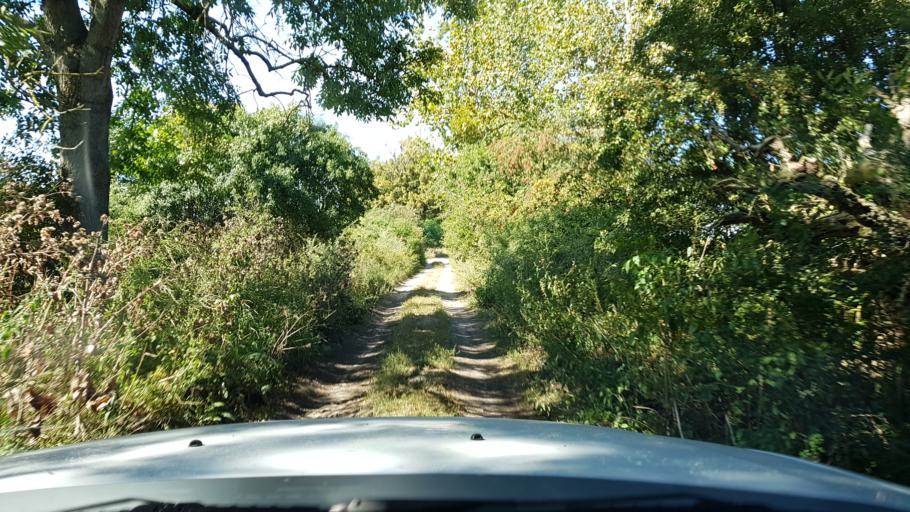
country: PL
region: West Pomeranian Voivodeship
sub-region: Powiat gryfinski
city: Cedynia
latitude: 52.8573
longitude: 14.2248
